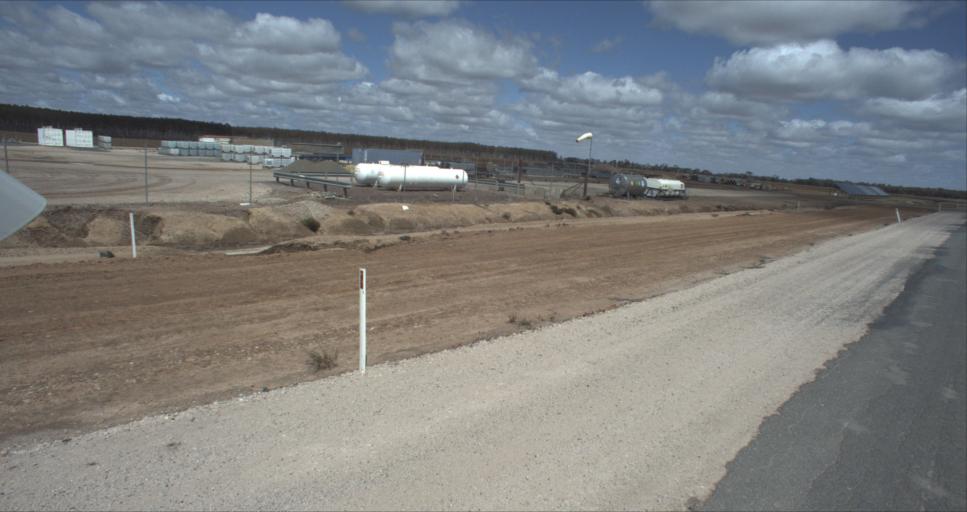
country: AU
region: New South Wales
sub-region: Murrumbidgee Shire
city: Darlington Point
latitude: -34.5761
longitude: 146.1781
